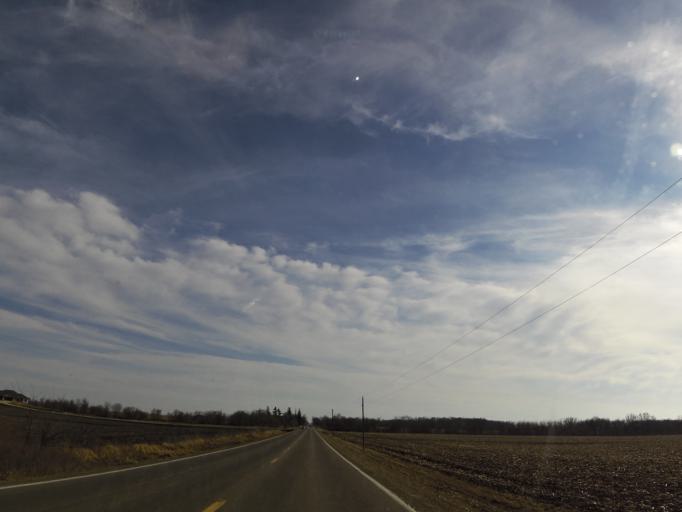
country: US
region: Minnesota
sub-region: Rice County
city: Northfield
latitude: 44.5264
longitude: -93.2004
